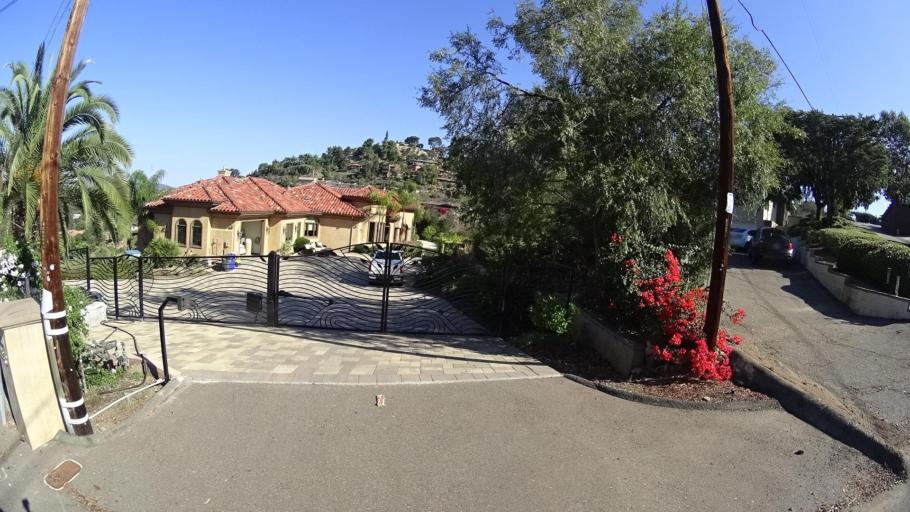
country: US
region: California
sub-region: San Diego County
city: Casa de Oro-Mount Helix
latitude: 32.7689
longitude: -116.9907
